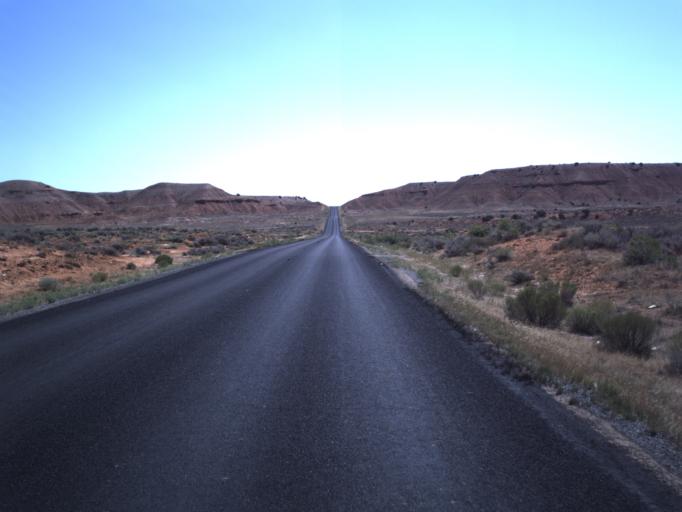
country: US
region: Utah
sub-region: Uintah County
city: Maeser
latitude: 40.4114
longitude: -109.7280
